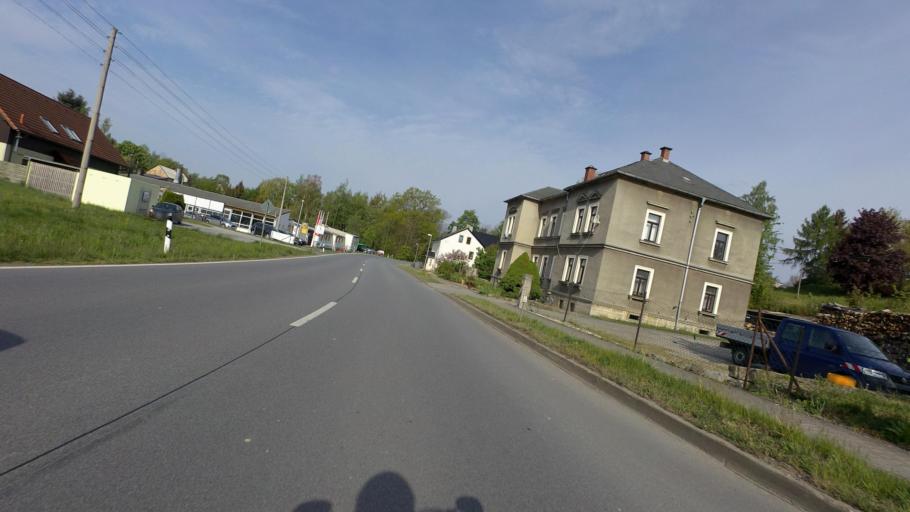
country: DE
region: Saxony
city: Stolpen
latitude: 51.0396
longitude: 14.1318
